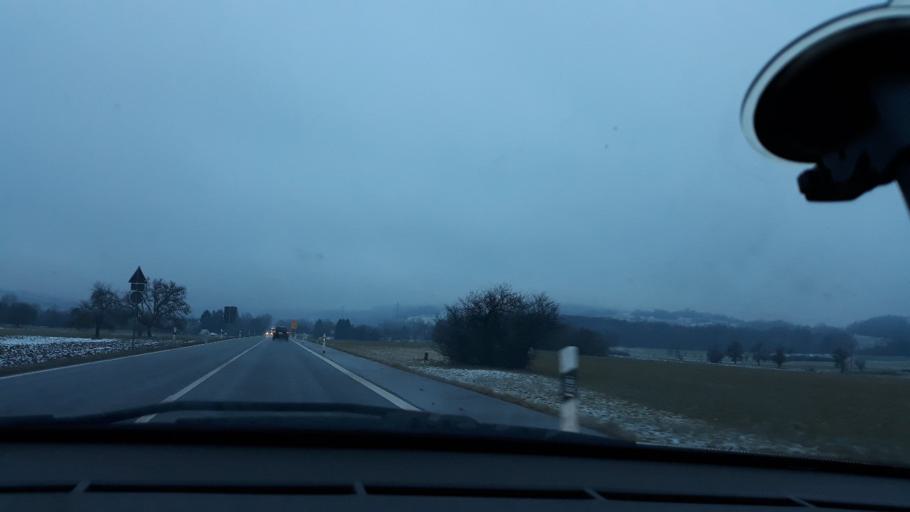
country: DE
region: Saarland
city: Gersheim
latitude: 49.2066
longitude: 7.1762
